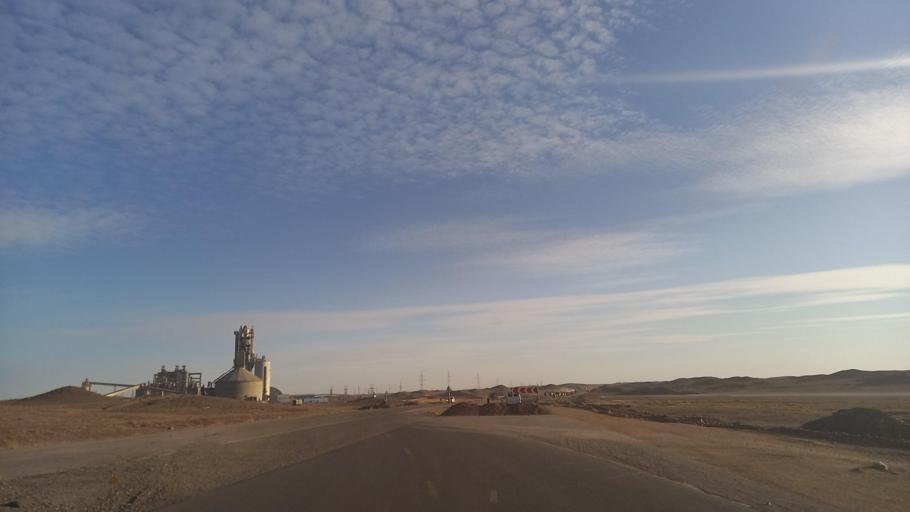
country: KZ
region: Zhambyl
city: Mynaral
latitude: 45.3945
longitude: 73.6436
